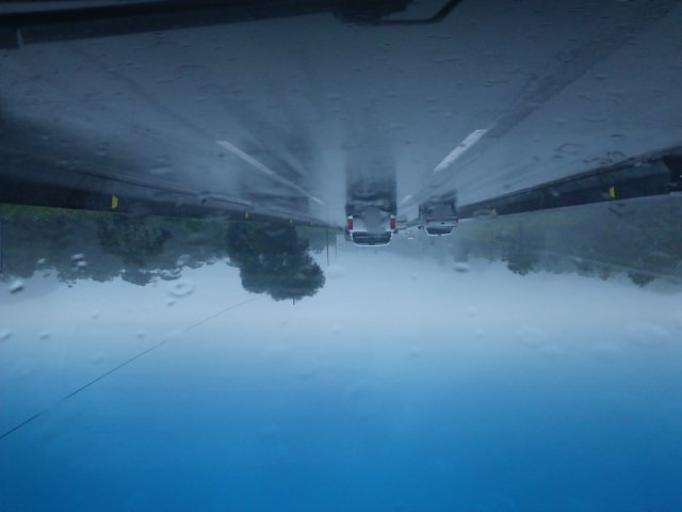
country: BR
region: Parana
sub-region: Guaratuba
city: Guaratuba
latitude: -25.8996
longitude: -48.9267
